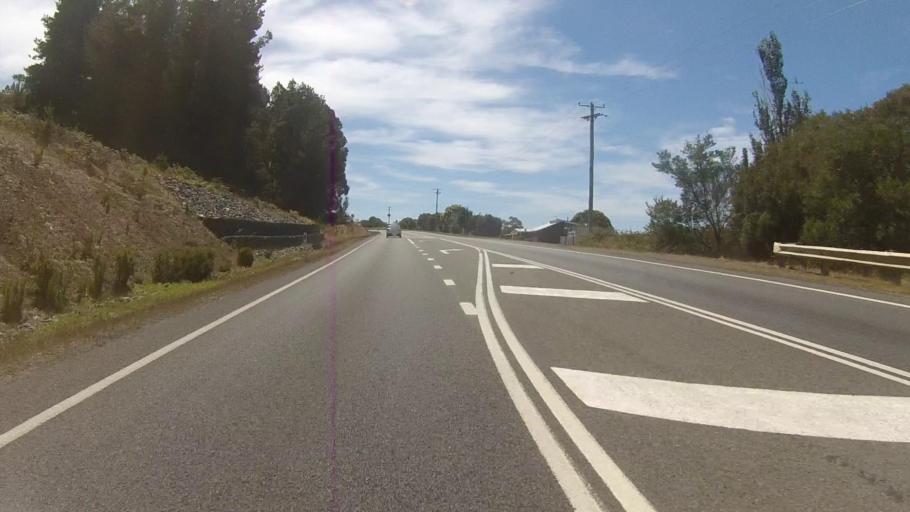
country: AU
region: Tasmania
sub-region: Kingborough
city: Margate
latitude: -43.0051
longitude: 147.2742
